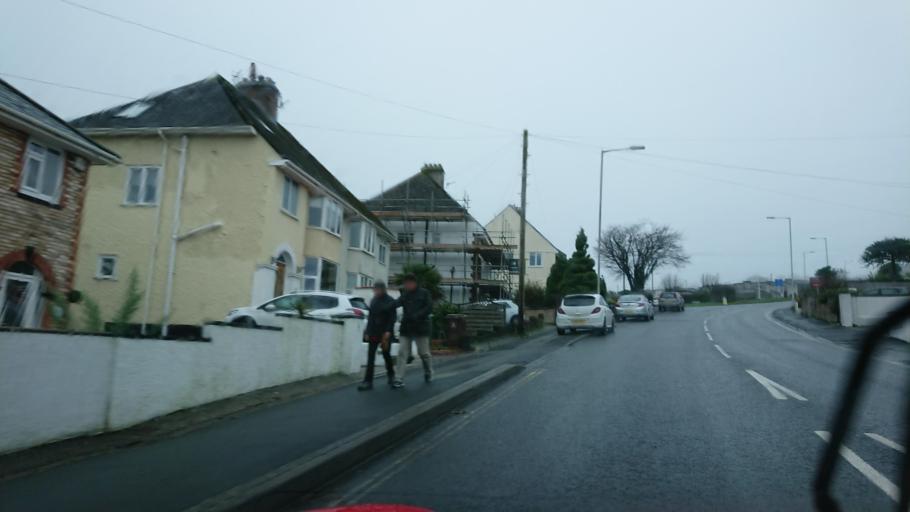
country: GB
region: England
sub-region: Plymouth
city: Plymstock
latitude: 50.3532
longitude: -4.1142
